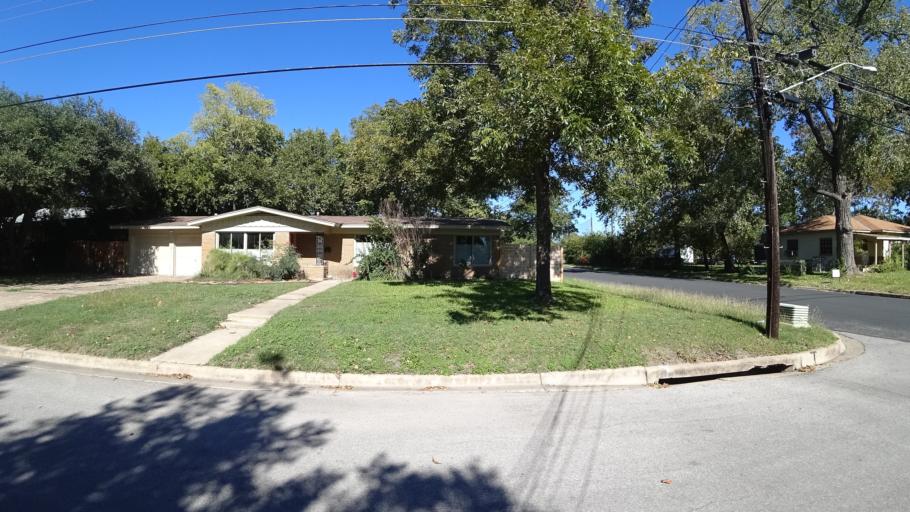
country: US
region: Texas
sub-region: Travis County
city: Austin
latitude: 30.3370
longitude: -97.7254
